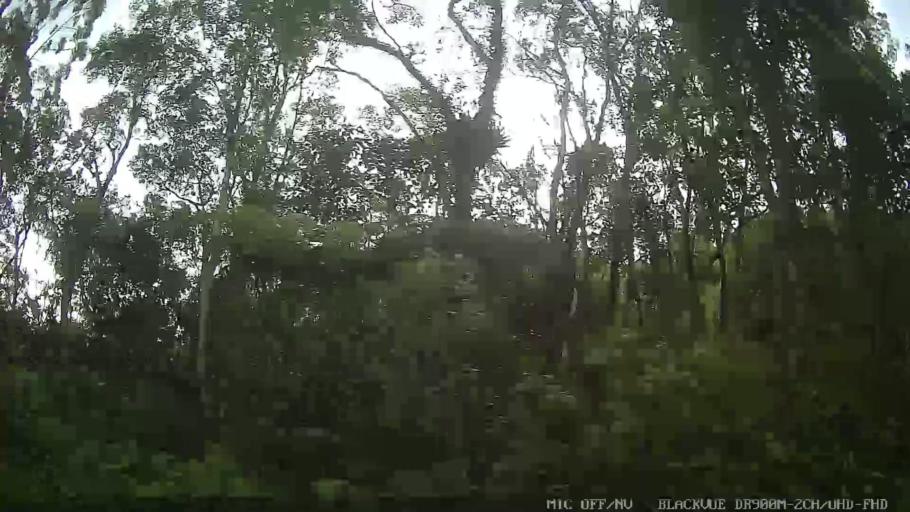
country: BR
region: Sao Paulo
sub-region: Santa Branca
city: Santa Branca
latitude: -23.5542
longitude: -45.6732
